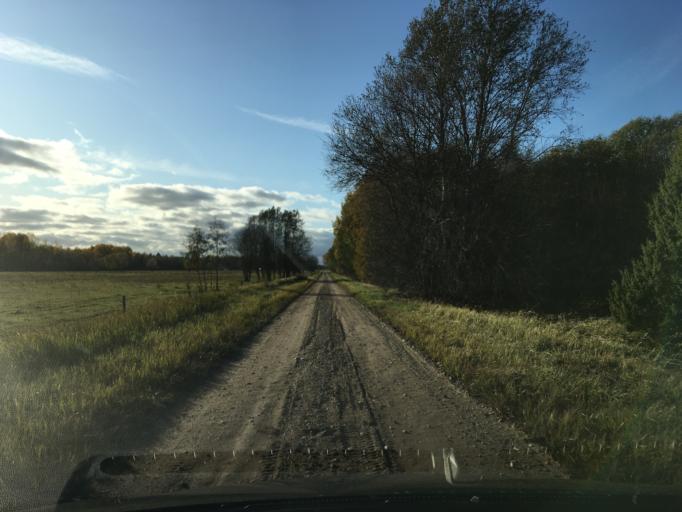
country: EE
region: Laeaene
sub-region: Lihula vald
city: Lihula
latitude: 58.5635
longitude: 23.8125
